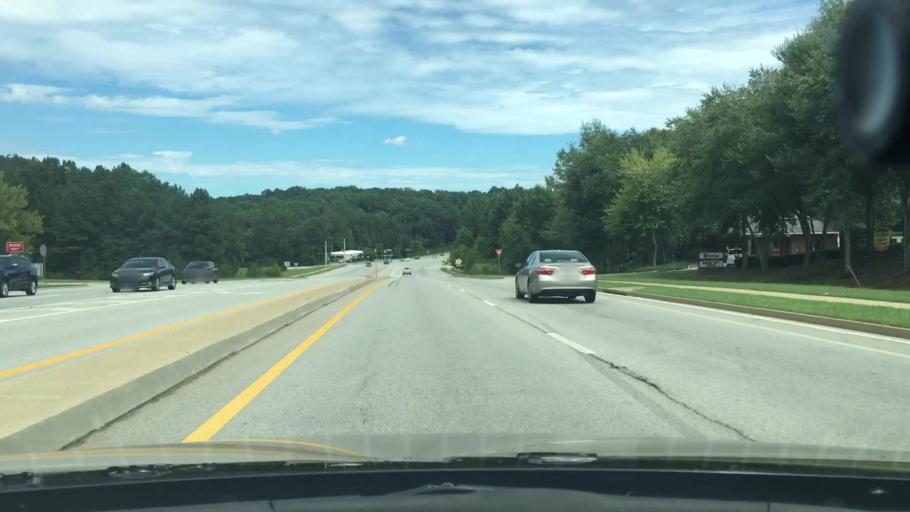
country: US
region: Georgia
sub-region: Coweta County
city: Newnan
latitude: 33.3990
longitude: -84.7875
